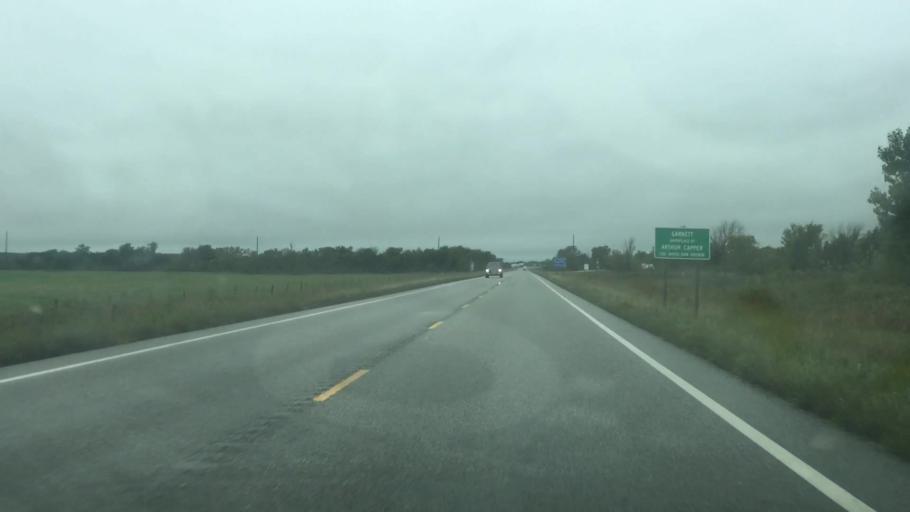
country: US
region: Kansas
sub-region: Anderson County
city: Garnett
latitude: 38.2906
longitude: -95.2038
